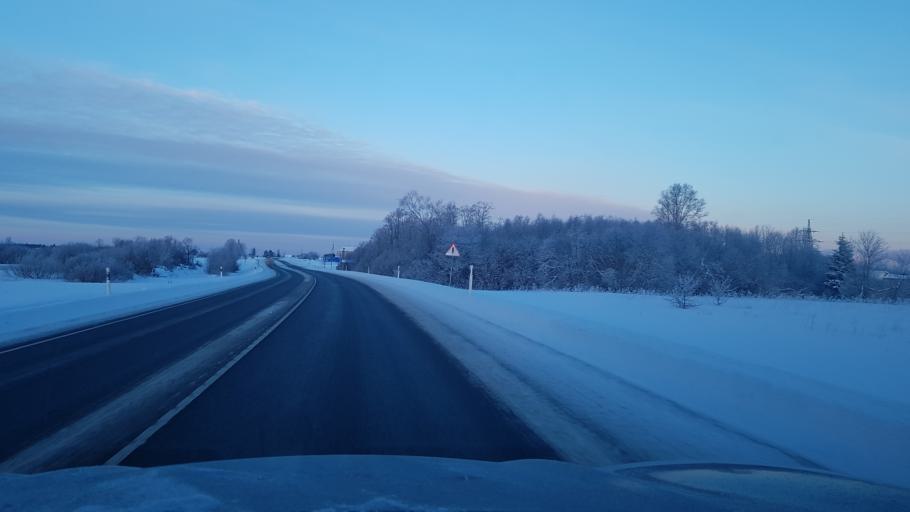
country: EE
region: Ida-Virumaa
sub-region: Narva-Joesuu linn
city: Narva-Joesuu
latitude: 59.4004
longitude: 28.0687
